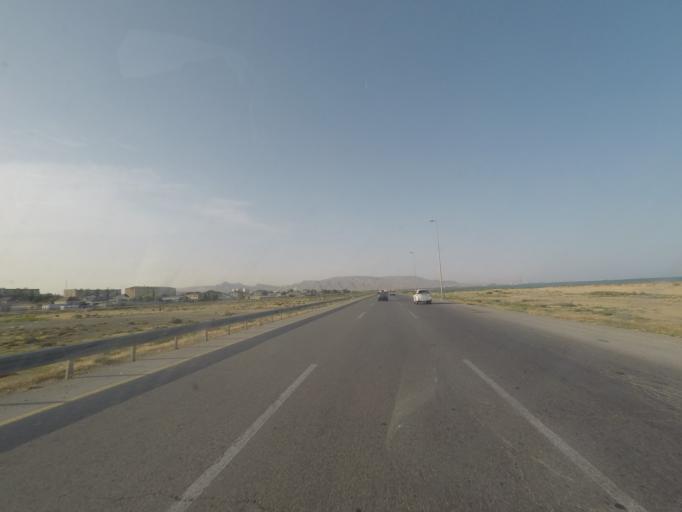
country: AZ
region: Baki
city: Qobustan
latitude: 40.1617
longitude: 49.4647
